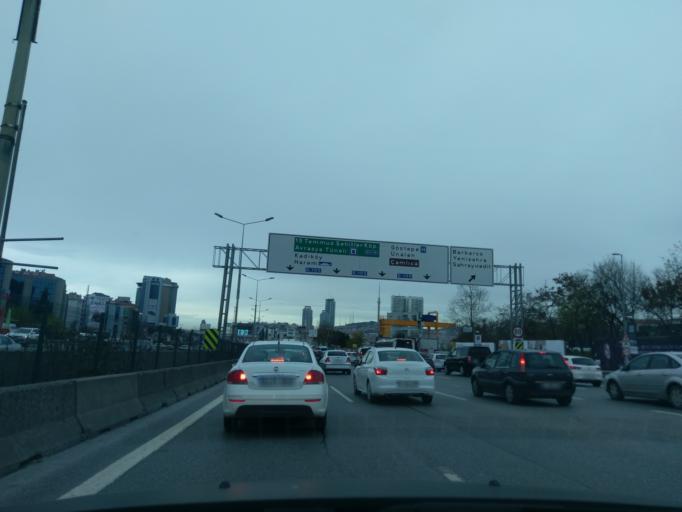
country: TR
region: Istanbul
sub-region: Atasehir
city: Atasehir
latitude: 40.9834
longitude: 29.0928
